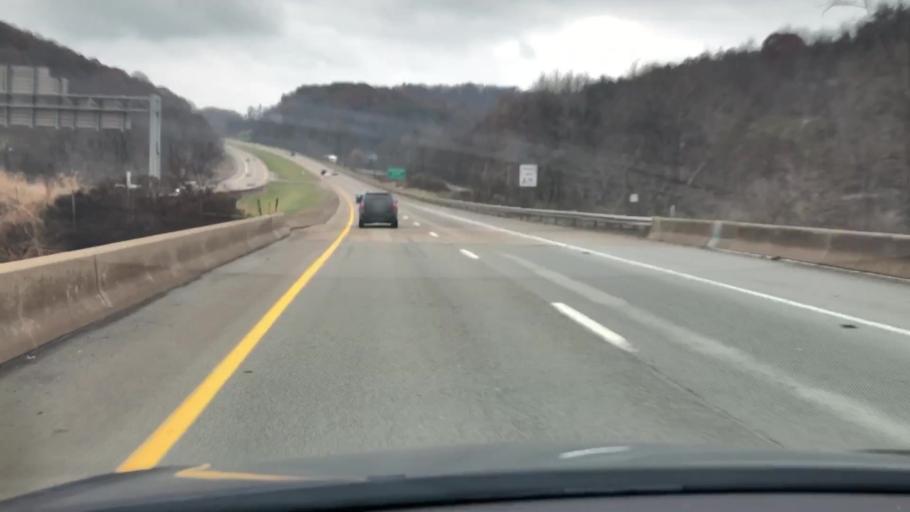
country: US
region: Pennsylvania
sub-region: Westmoreland County
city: New Stanton
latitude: 40.2116
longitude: -79.5901
